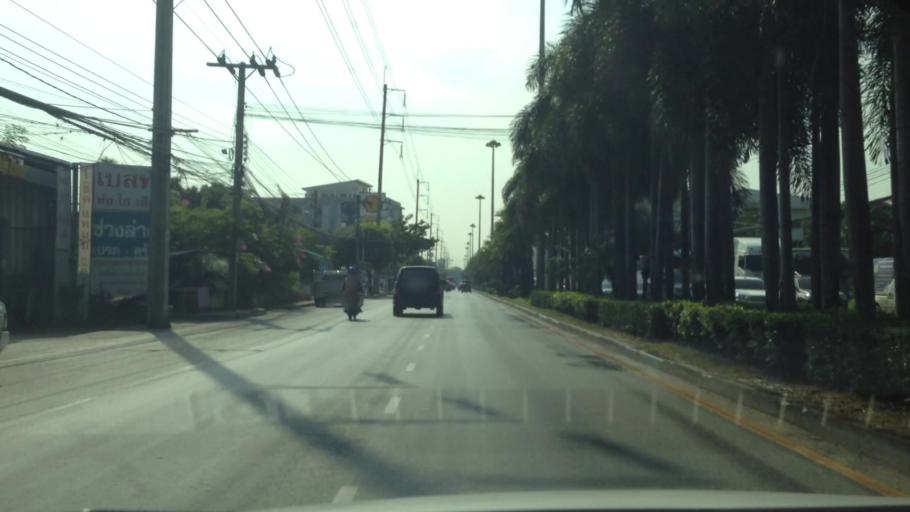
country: TH
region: Samut Prakan
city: Samut Prakan
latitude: 13.5822
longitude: 100.6012
